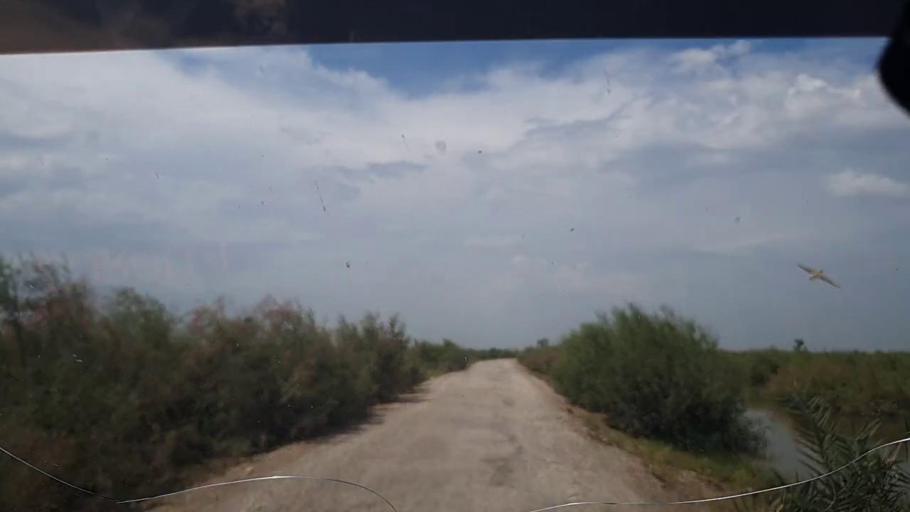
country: PK
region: Sindh
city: Ghauspur
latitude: 28.1464
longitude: 68.9813
